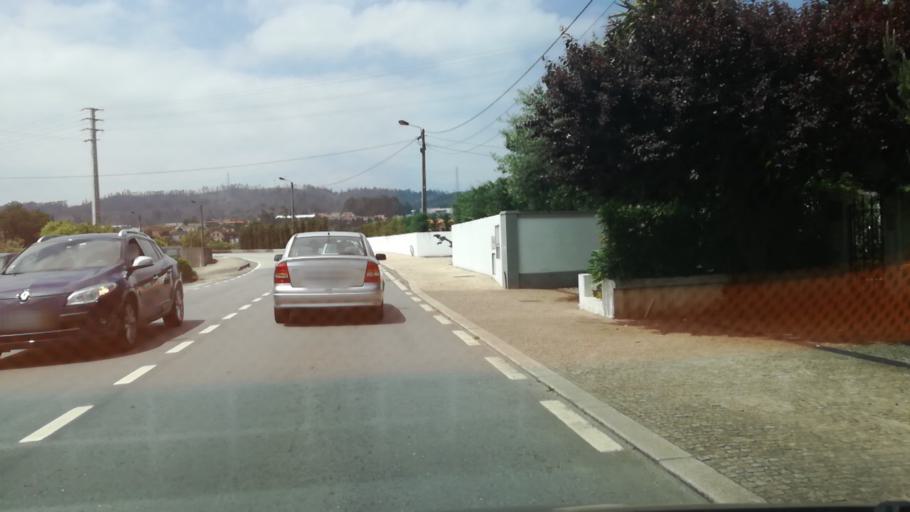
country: PT
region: Porto
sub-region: Trofa
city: Bougado
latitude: 41.3226
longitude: -8.5719
